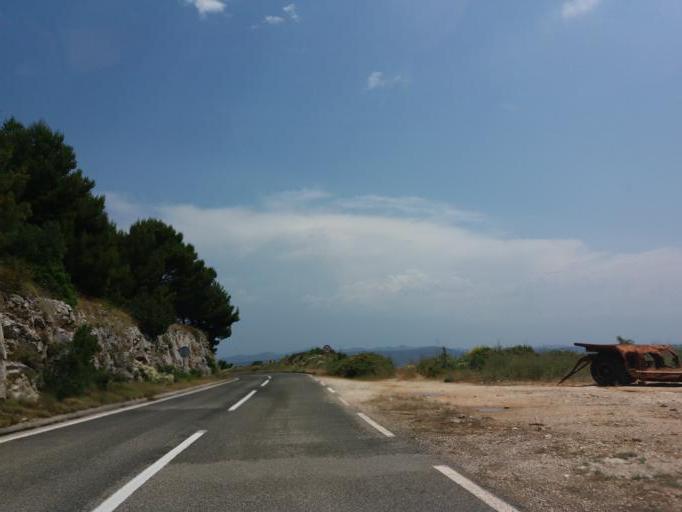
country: HR
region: Zadarska
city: Ugljan
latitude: 44.0495
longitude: 15.0149
